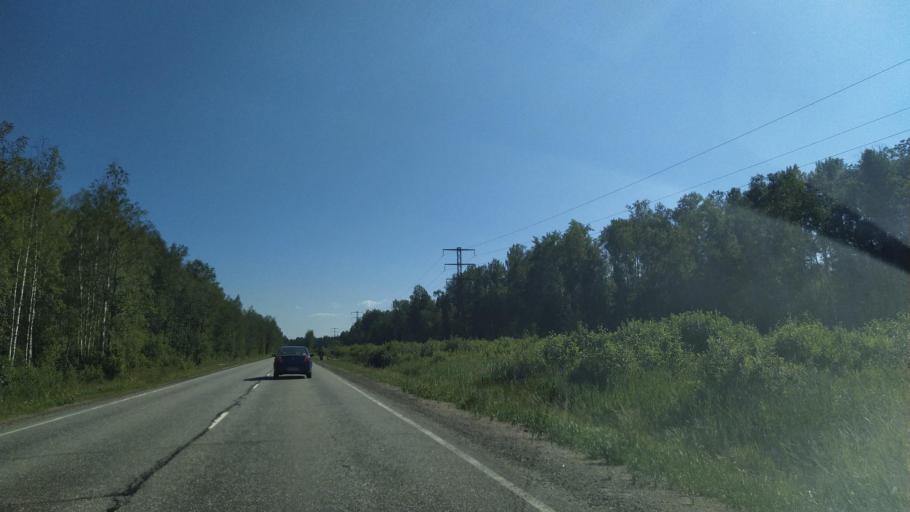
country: RU
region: Leningrad
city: Imeni Morozova
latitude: 60.0211
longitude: 31.0368
